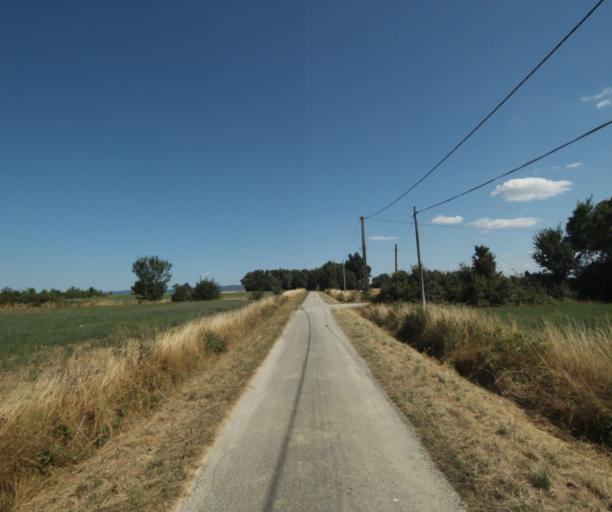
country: FR
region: Midi-Pyrenees
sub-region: Departement de la Haute-Garonne
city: Saint-Felix-Lauragais
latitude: 43.4751
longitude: 1.9043
